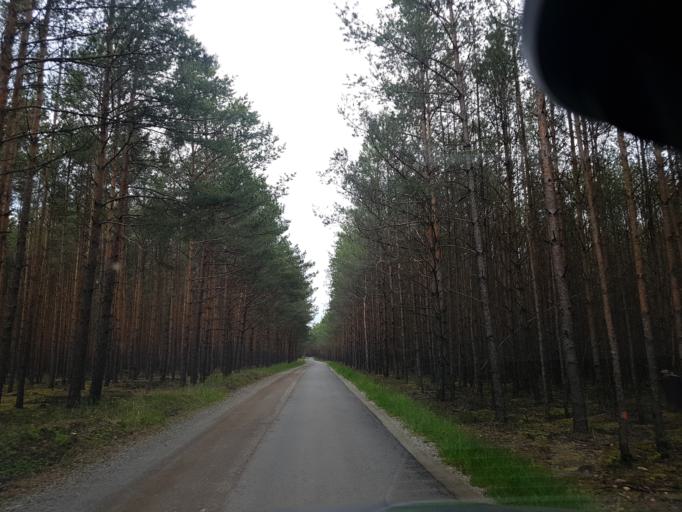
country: DE
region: Brandenburg
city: Crinitz
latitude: 51.6820
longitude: 13.7793
